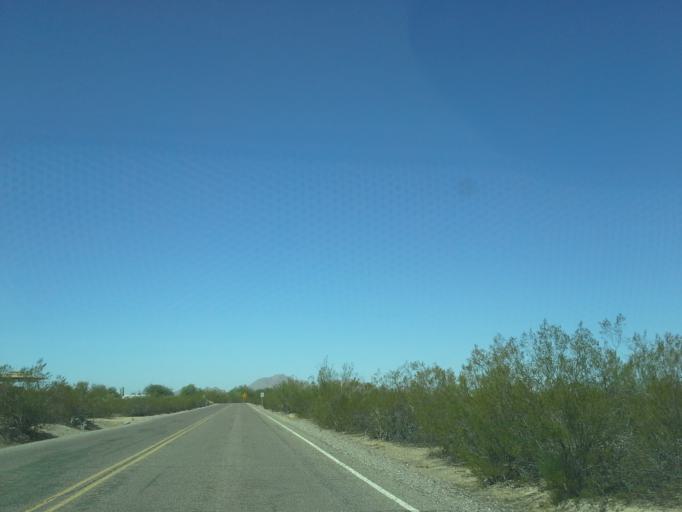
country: US
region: Arizona
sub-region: Pinal County
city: Coolidge
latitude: 32.9955
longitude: -111.5329
